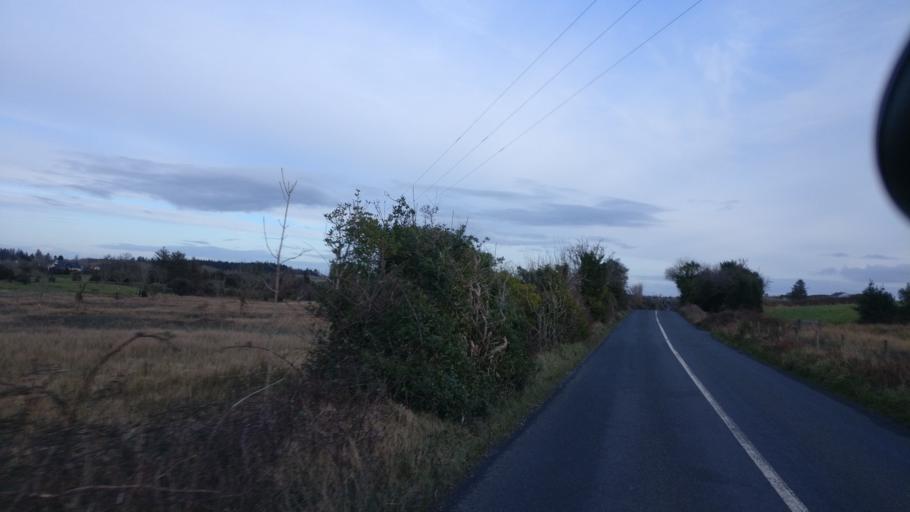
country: IE
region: Connaught
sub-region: County Galway
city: Oughterard
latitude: 53.5323
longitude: -9.3462
